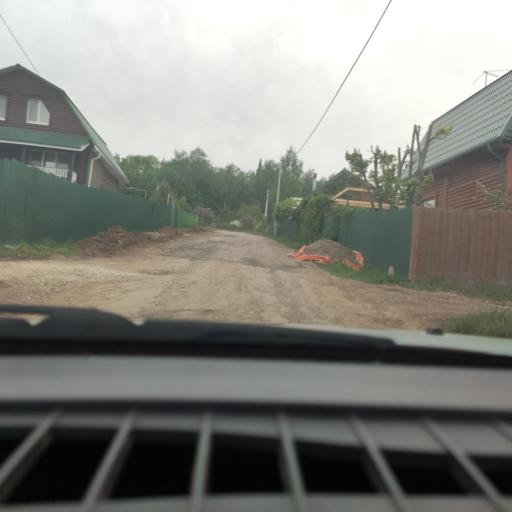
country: RU
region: Perm
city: Novyye Lyady
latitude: 57.8910
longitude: 56.6619
